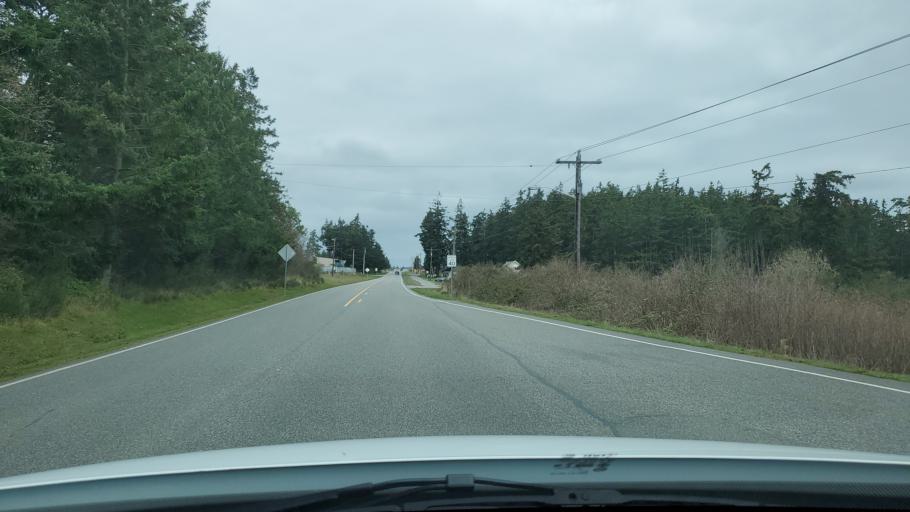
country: US
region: Washington
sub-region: Island County
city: Oak Harbor
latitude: 48.3139
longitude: -122.6304
